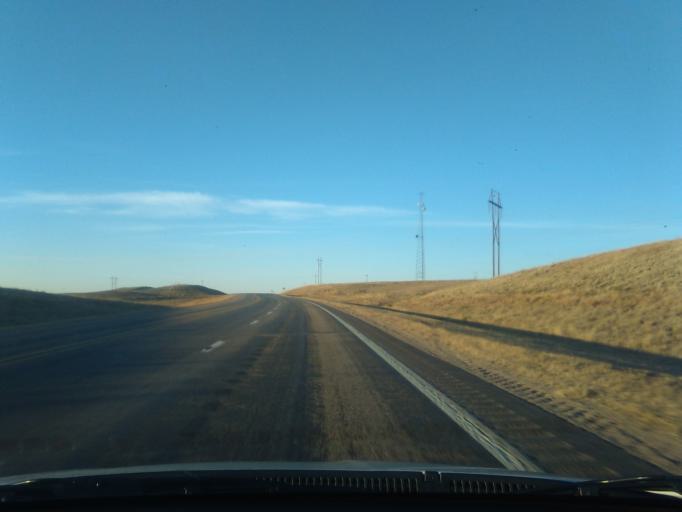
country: US
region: Nebraska
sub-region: Cheyenne County
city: Sidney
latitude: 41.1591
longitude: -102.9475
